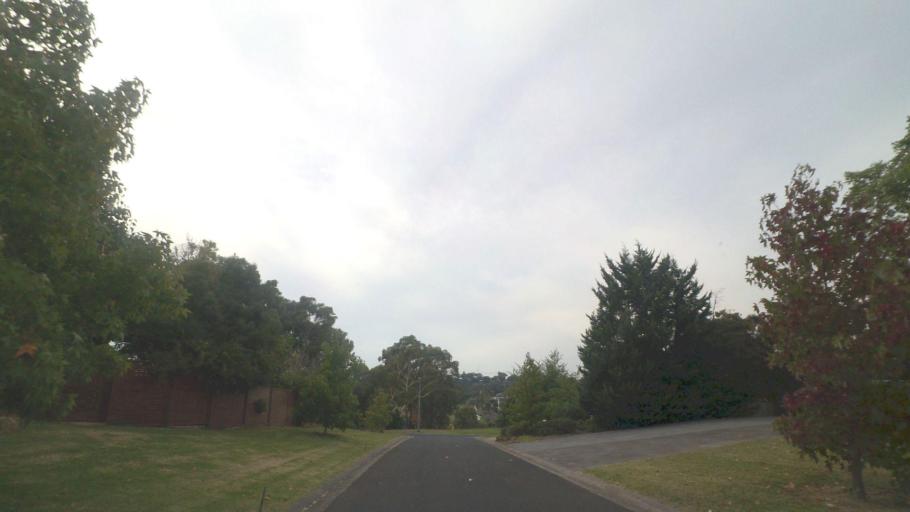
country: AU
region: Victoria
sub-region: Manningham
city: Park Orchards
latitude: -37.7655
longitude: 145.1935
